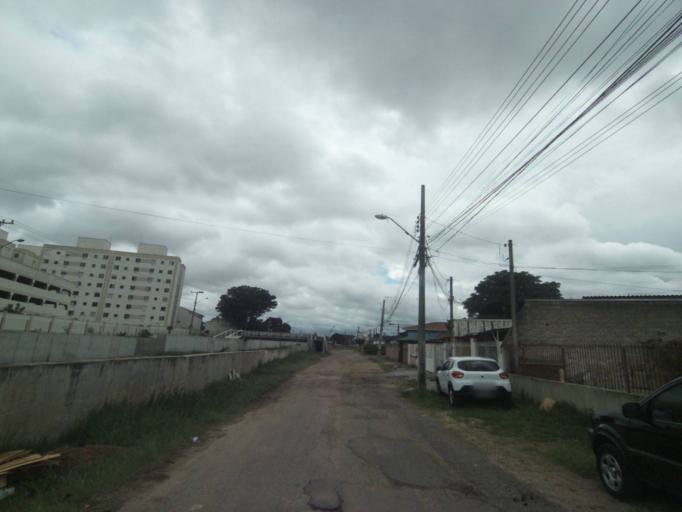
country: BR
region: Parana
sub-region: Curitiba
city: Curitiba
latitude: -25.4790
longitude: -49.2718
